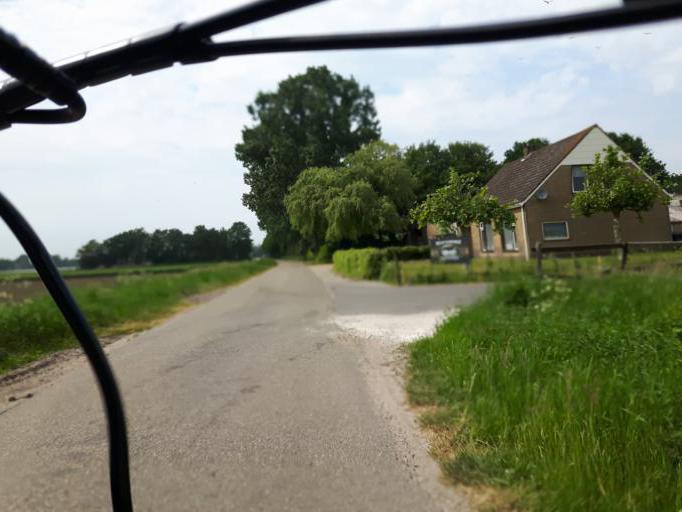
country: NL
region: North Brabant
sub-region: Gemeente Steenbergen
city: Welberg
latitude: 51.5368
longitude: 4.3240
